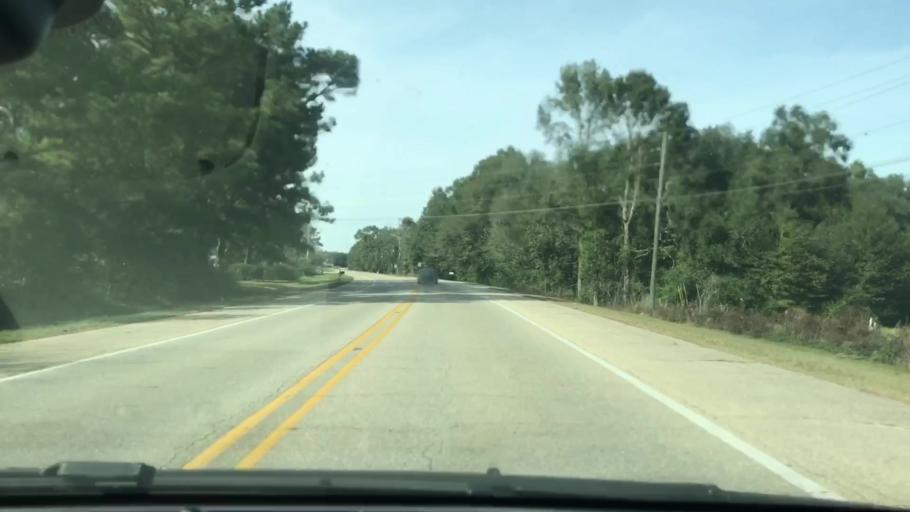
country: US
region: Louisiana
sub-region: Saint Tammany Parish
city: Pearl River
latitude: 30.4588
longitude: -89.8042
